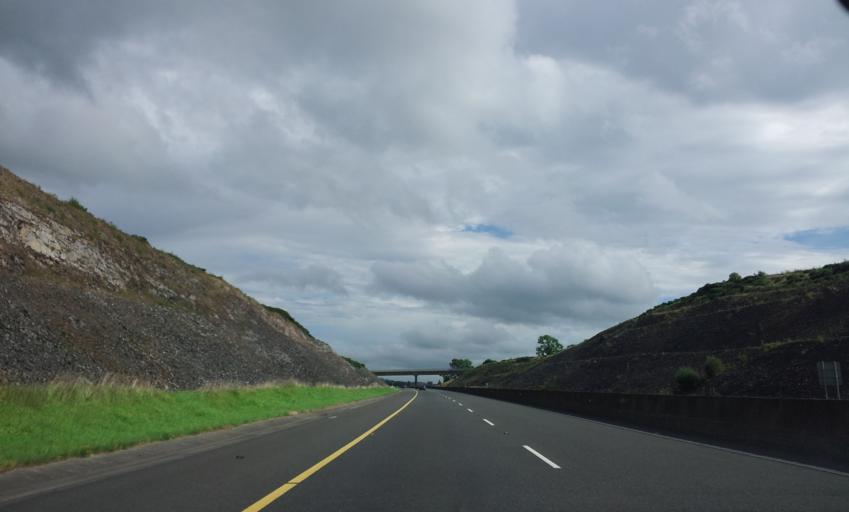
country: IE
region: Munster
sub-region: North Tipperary
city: Newport
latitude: 52.7673
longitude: -8.3892
